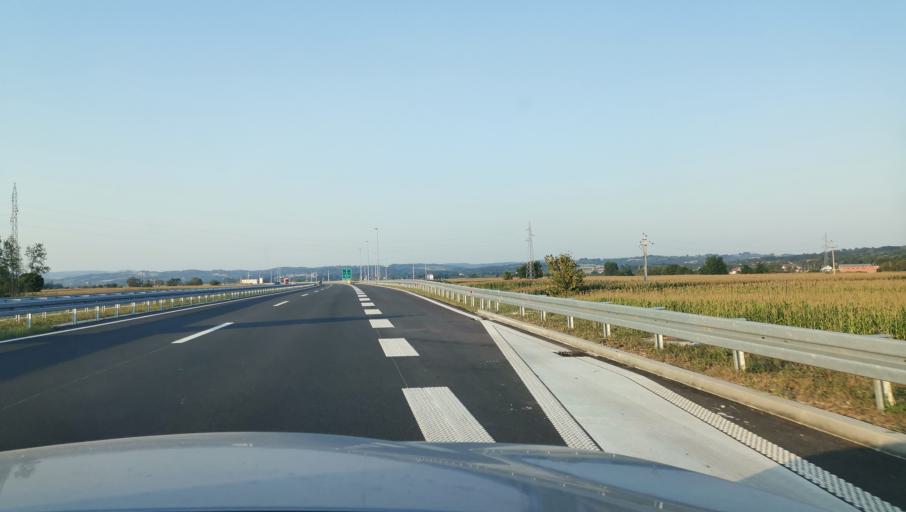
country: RS
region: Central Serbia
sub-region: Kolubarski Okrug
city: Ljig
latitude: 44.2388
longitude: 20.2595
